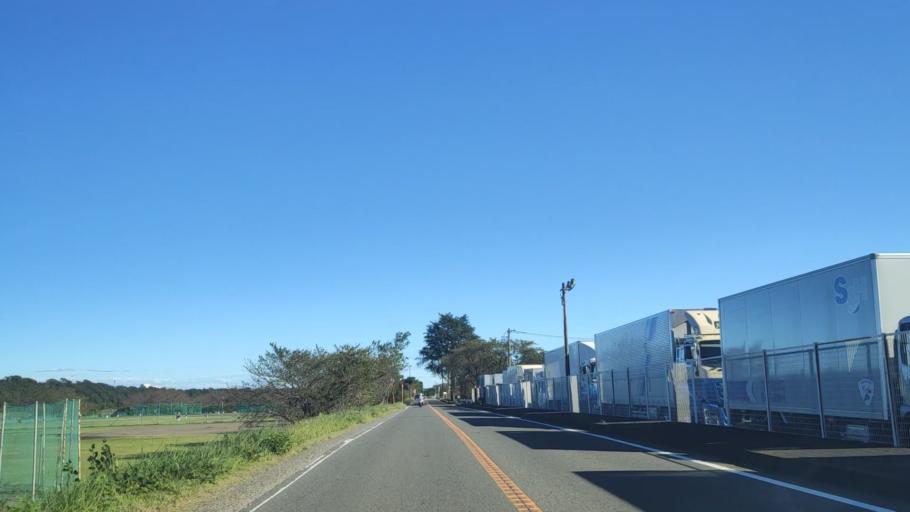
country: JP
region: Kanagawa
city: Zama
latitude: 35.5381
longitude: 139.3316
